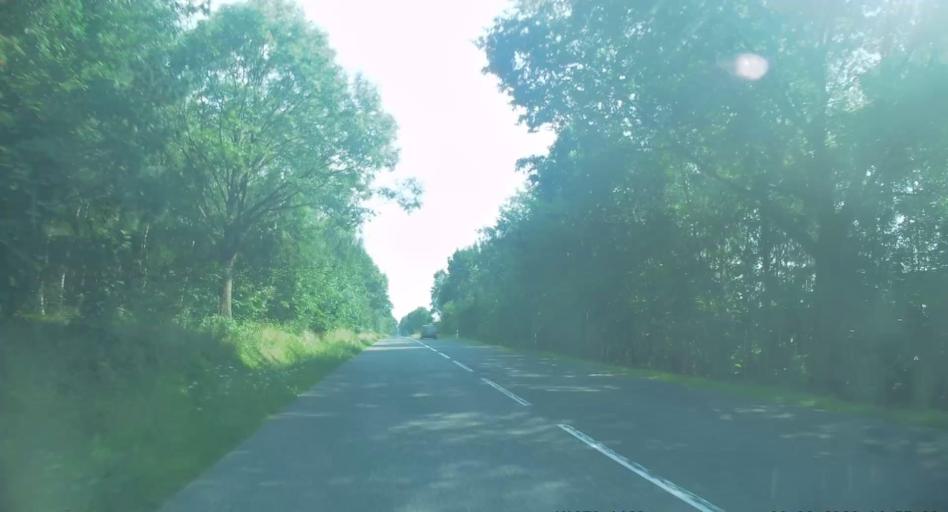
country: PL
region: Swietokrzyskie
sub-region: Powiat kielecki
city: Lopuszno
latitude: 50.9271
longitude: 20.2392
